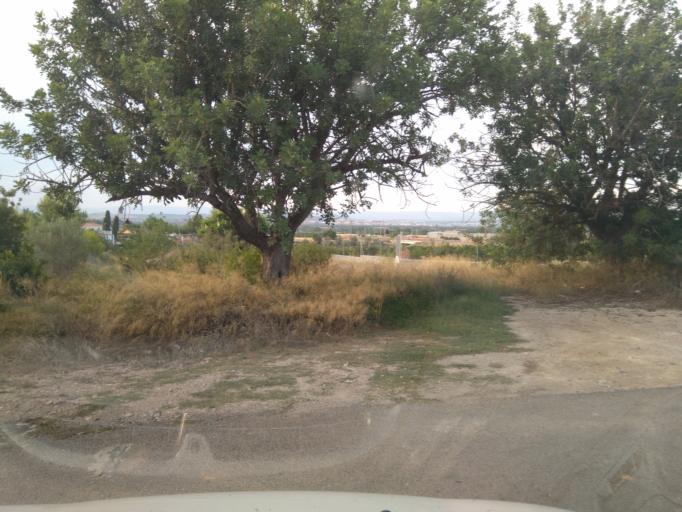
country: ES
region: Valencia
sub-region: Provincia de Valencia
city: Ribarroja
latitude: 39.5461
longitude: -0.5862
